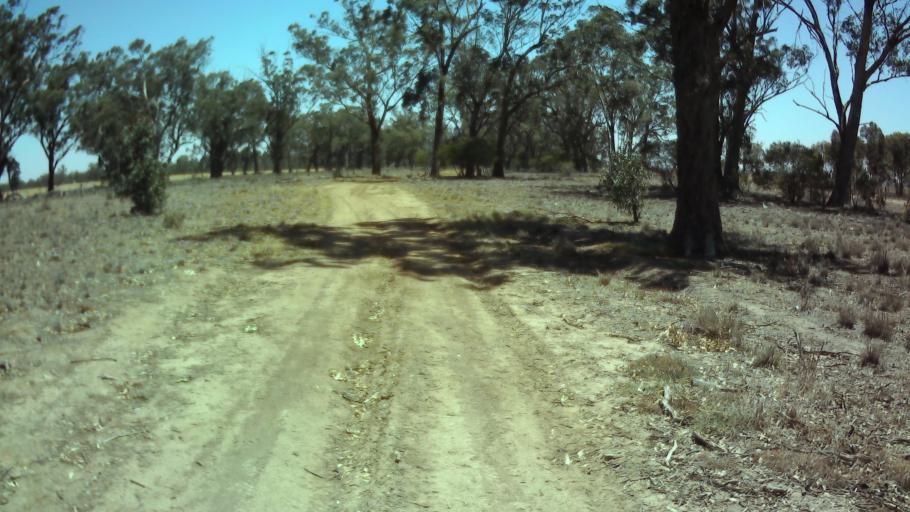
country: AU
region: New South Wales
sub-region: Weddin
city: Grenfell
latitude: -34.0576
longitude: 147.8175
